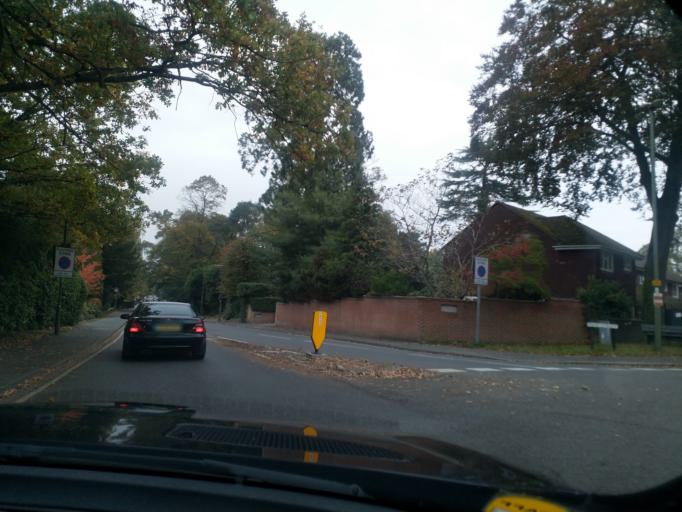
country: GB
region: England
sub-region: Surrey
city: Camberley
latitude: 51.3327
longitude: -0.7464
